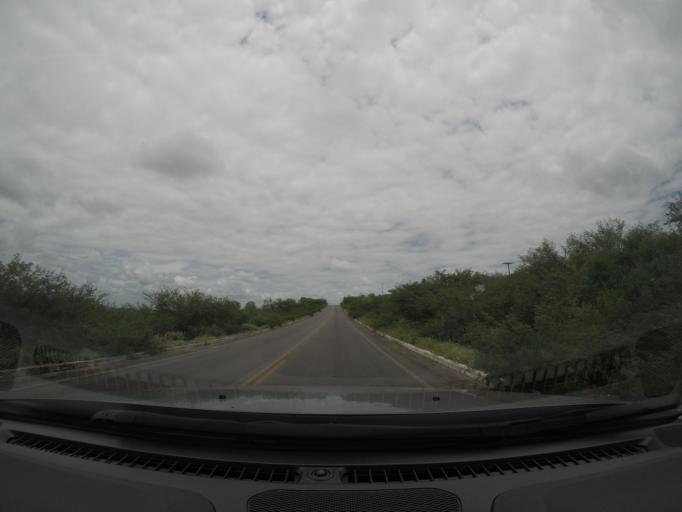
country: BR
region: Bahia
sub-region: Itaberaba
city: Itaberaba
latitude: -12.4970
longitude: -40.2407
